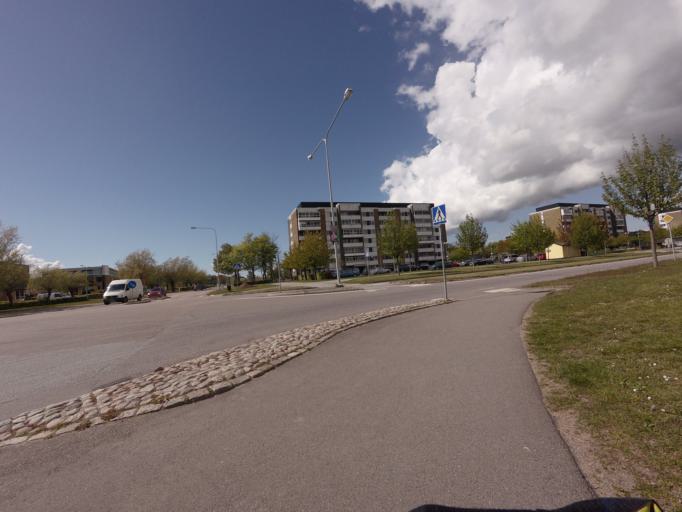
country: SE
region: Skane
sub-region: Landskrona
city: Landskrona
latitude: 55.8891
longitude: 12.8504
